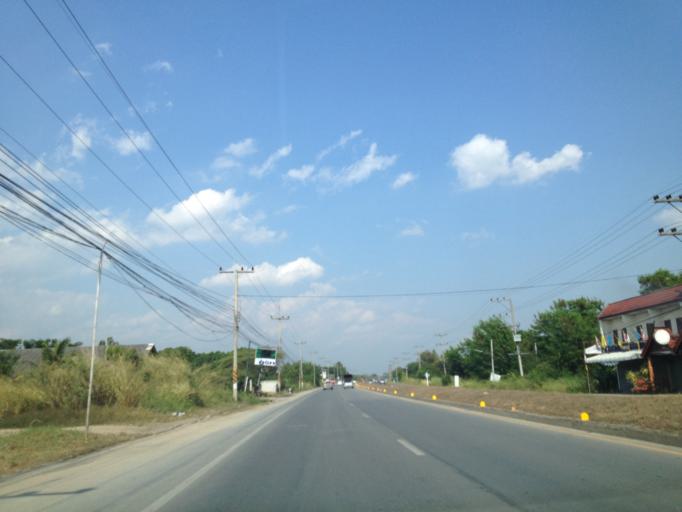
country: TH
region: Lamphun
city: Pa Sang
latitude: 18.5429
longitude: 98.8644
